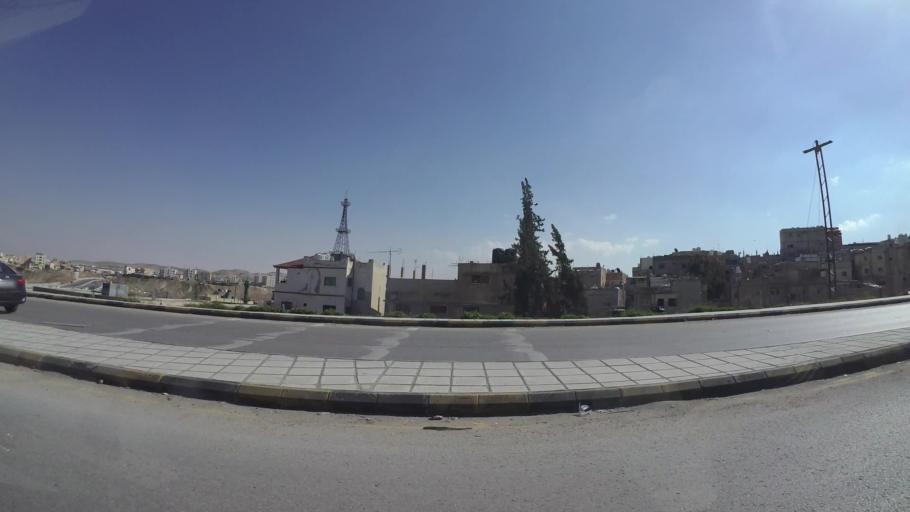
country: JO
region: Zarqa
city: Russeifa
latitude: 32.0262
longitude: 36.0687
